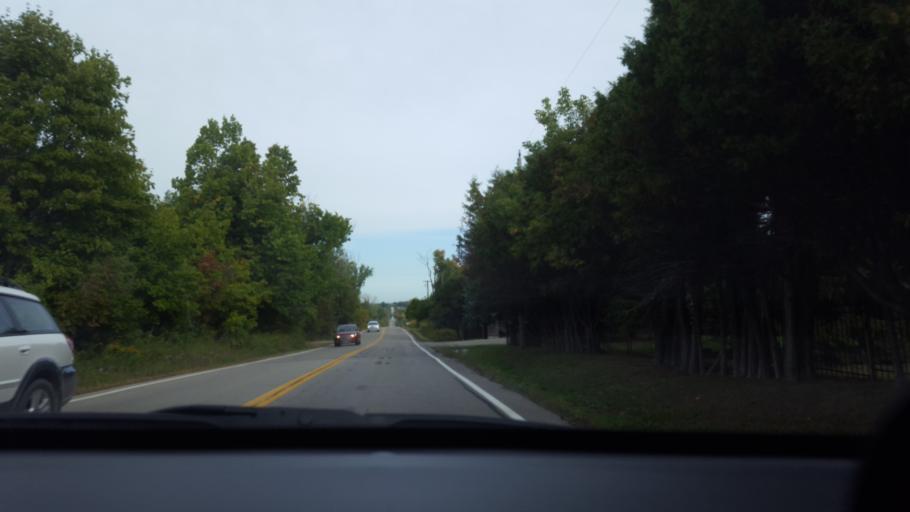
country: CA
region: Ontario
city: Newmarket
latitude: 43.9897
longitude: -79.5447
